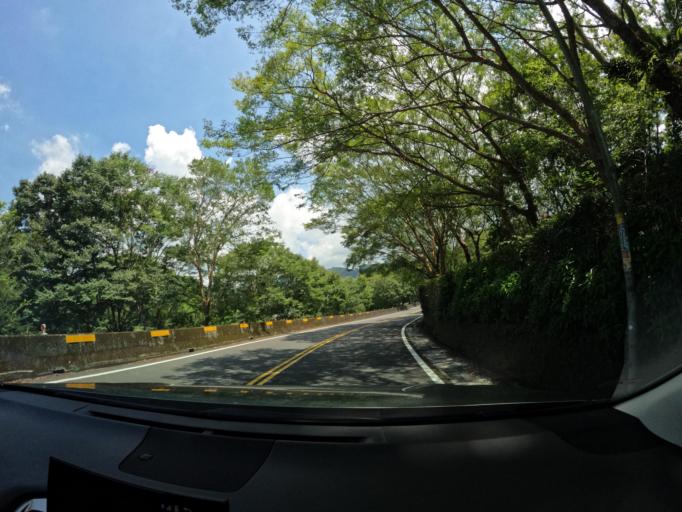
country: TW
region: Taiwan
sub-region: Miaoli
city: Miaoli
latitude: 24.4084
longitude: 120.7890
